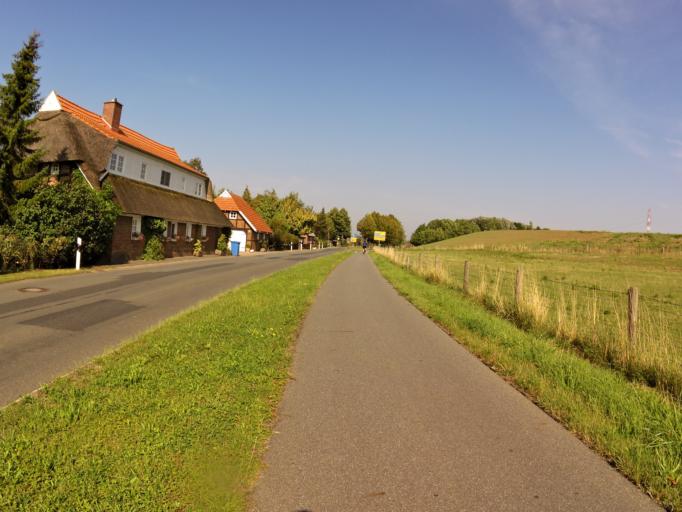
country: DE
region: Lower Saxony
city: Neuenkirchen
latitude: 53.1916
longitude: 8.5051
